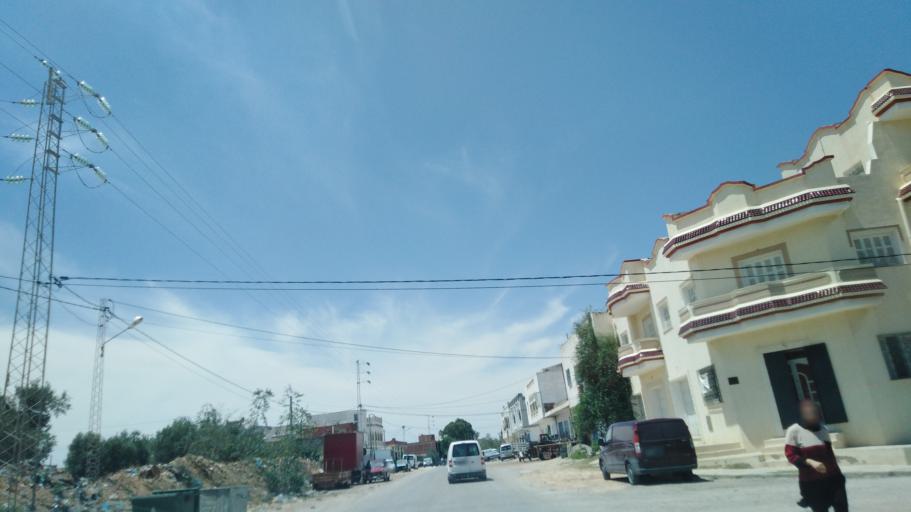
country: TN
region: Al Mahdiyah
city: Ksour Essaf
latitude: 35.4154
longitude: 10.9789
